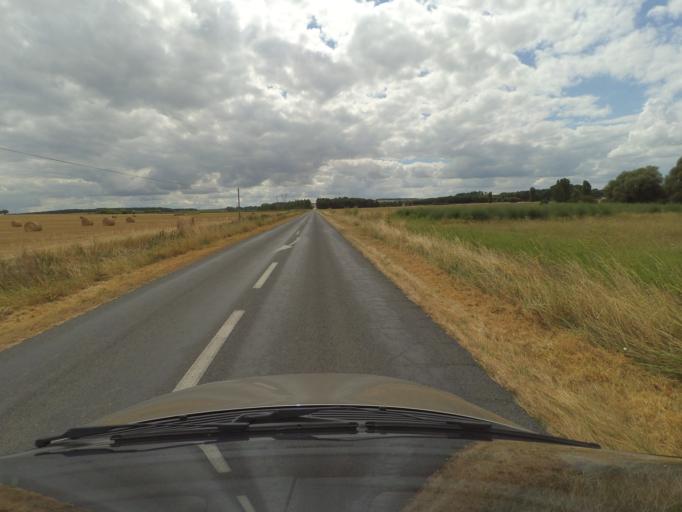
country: FR
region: Poitou-Charentes
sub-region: Departement de la Vienne
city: Saint-Gervais-les-Trois-Clochers
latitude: 46.9416
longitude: 0.4203
